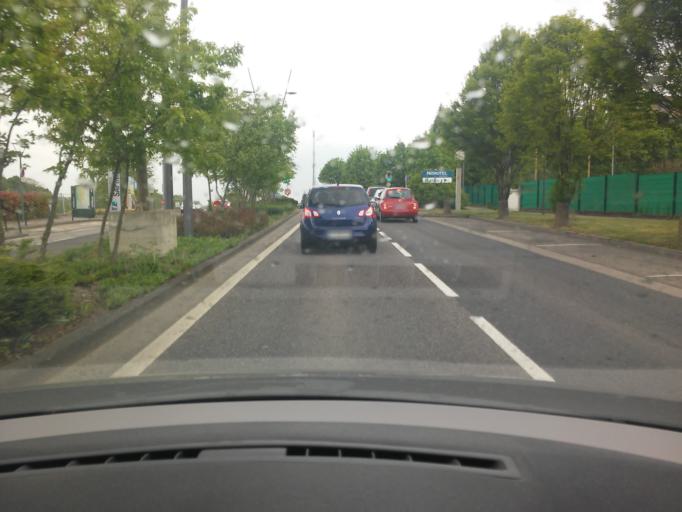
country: FR
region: Lorraine
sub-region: Departement de Meurthe-et-Moselle
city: Laxou
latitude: 48.6950
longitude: 6.1254
